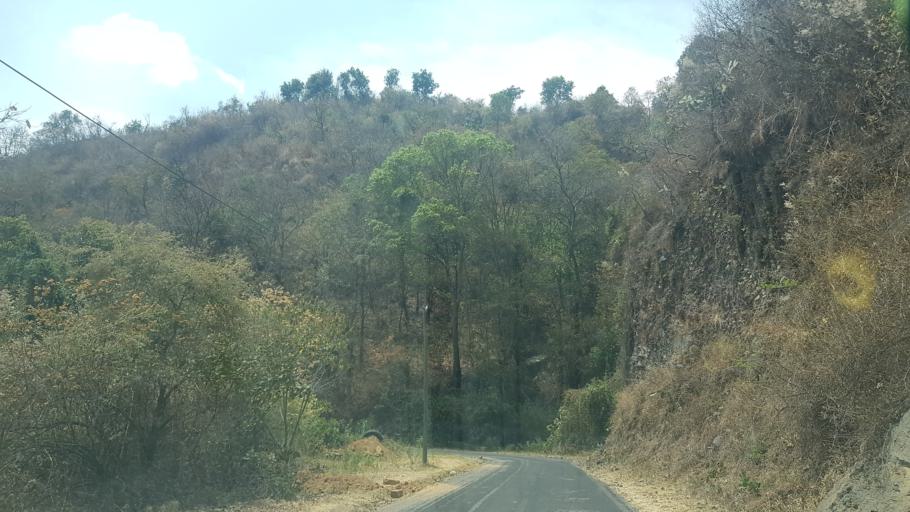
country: MX
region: Puebla
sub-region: Tochimilco
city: La Magdalena Yancuitlalpan
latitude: 18.8753
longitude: -98.6114
